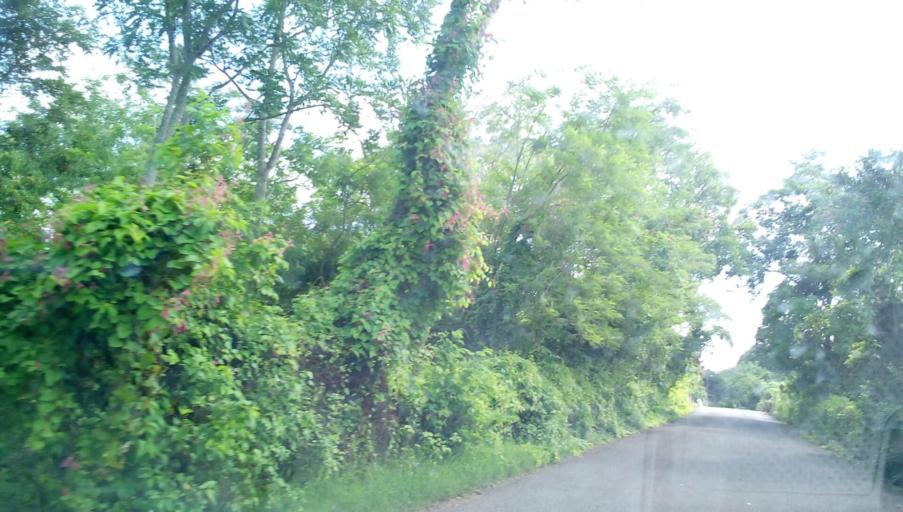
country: MX
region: Veracruz
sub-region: Citlaltepetl
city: Las Sabinas
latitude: 21.3639
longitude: -97.9019
